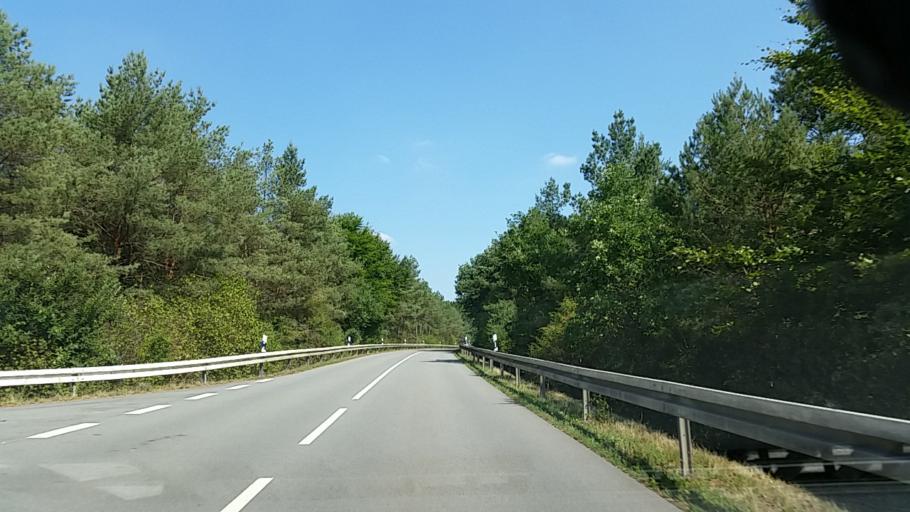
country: DE
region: Lower Saxony
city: Vastorf
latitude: 53.1700
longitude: 10.5162
